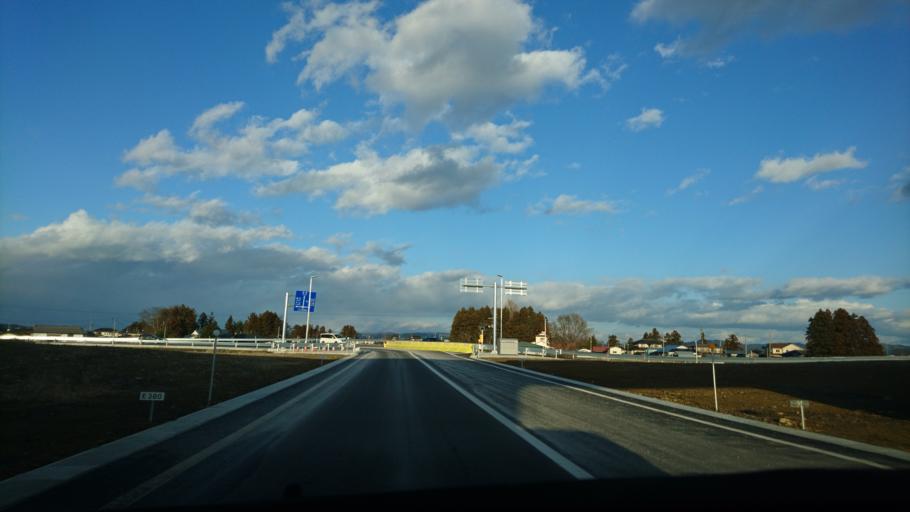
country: JP
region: Miyagi
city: Wakuya
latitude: 38.6946
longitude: 141.2147
